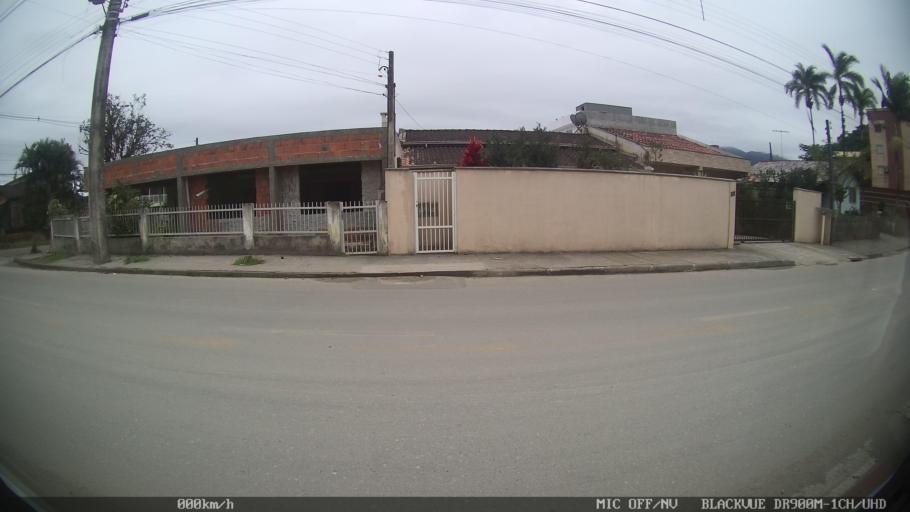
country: BR
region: Santa Catarina
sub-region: Joinville
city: Joinville
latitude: -26.2751
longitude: -48.9012
